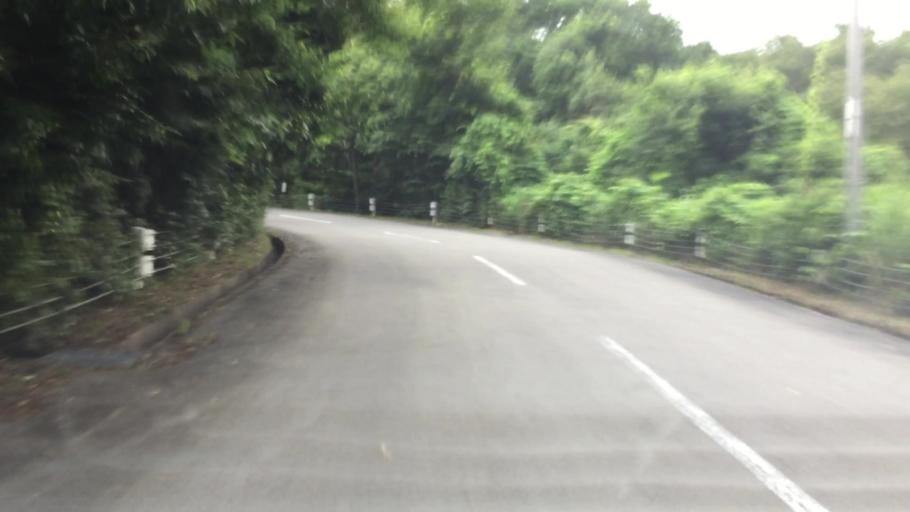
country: JP
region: Tochigi
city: Kuroiso
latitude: 37.1056
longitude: 140.0424
